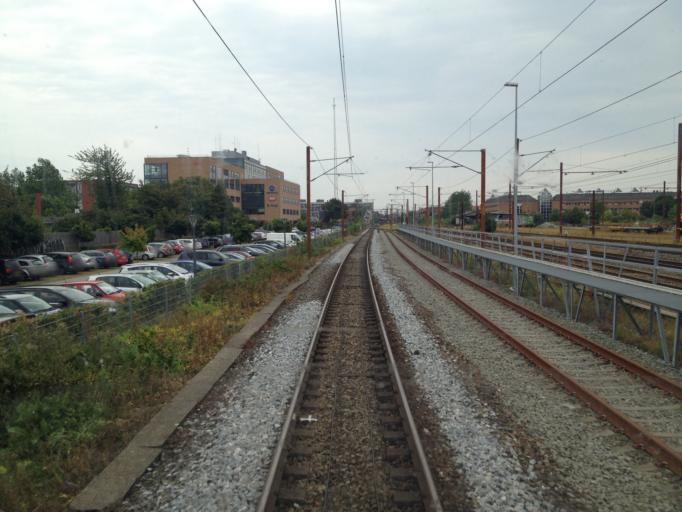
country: DK
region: Capital Region
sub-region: Glostrup Kommune
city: Glostrup
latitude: 55.6625
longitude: 12.3924
